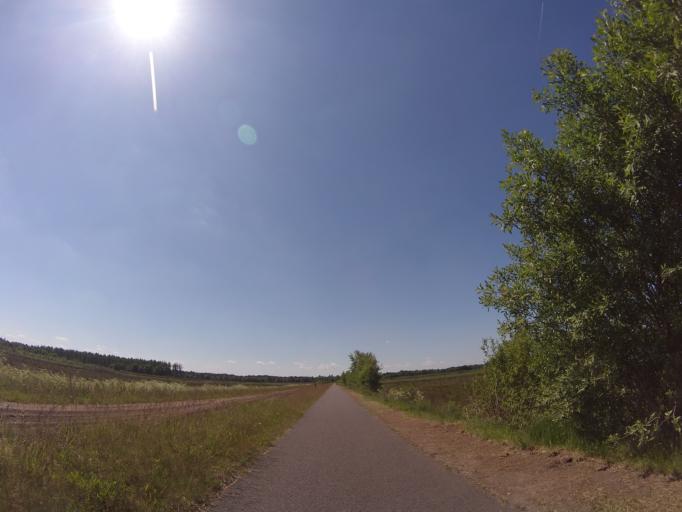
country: NL
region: Drenthe
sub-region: Gemeente Hoogeveen
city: Hoogeveen
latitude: 52.7672
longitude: 6.5740
